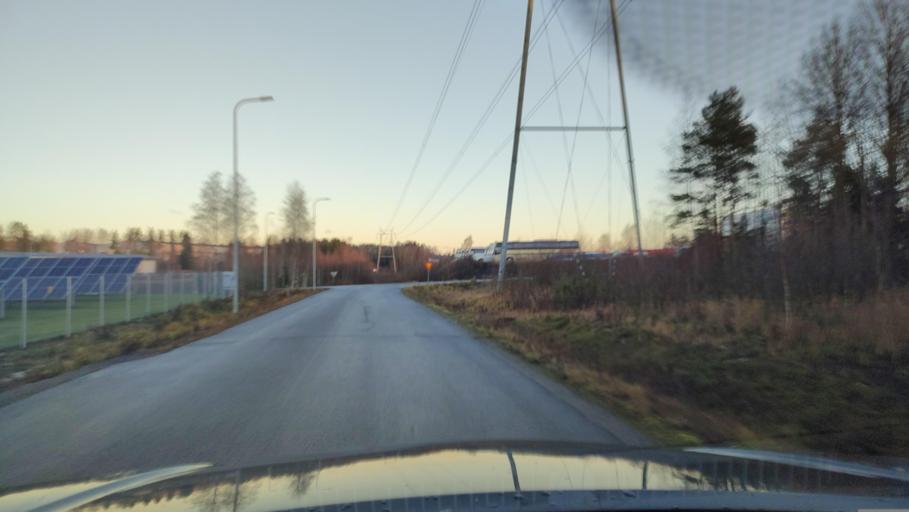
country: FI
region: Ostrobothnia
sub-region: Sydosterbotten
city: Naerpes
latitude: 62.4764
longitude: 21.3790
